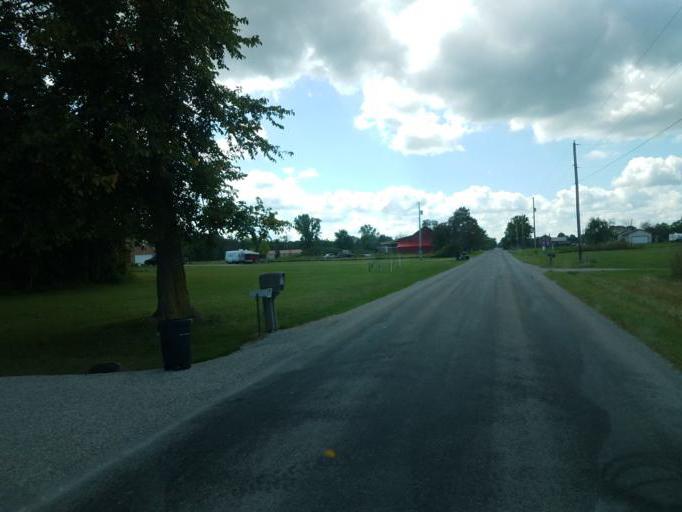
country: US
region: Ohio
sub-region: Medina County
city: Lodi
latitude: 41.0913
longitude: -82.0947
